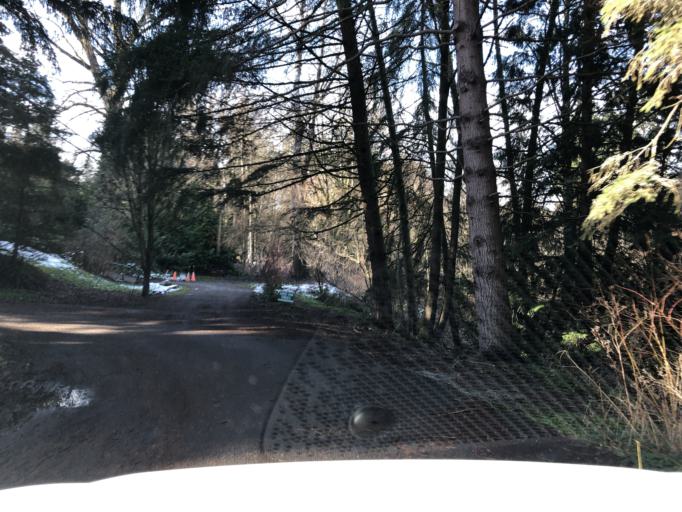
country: US
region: Washington
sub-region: King County
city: Shoreline
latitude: 47.7231
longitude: -122.3165
